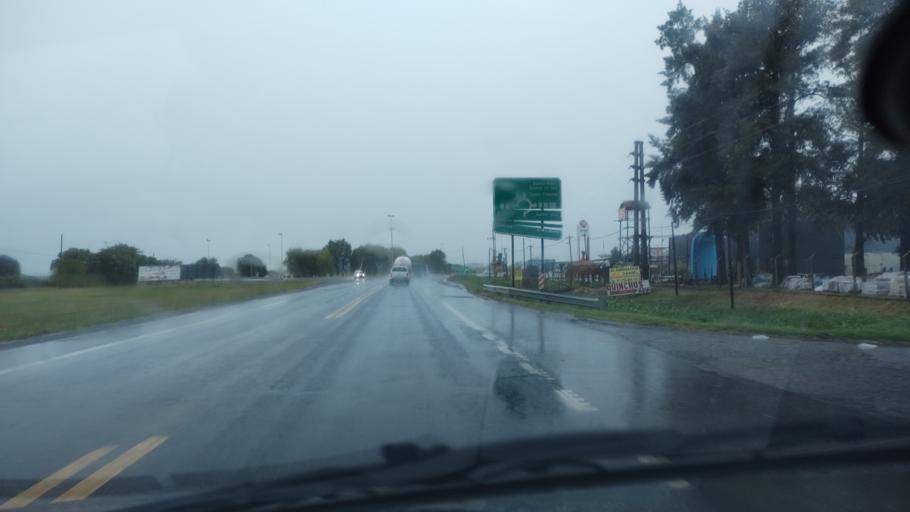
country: AR
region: Buenos Aires
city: Canuelas
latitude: -35.0279
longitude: -58.7467
